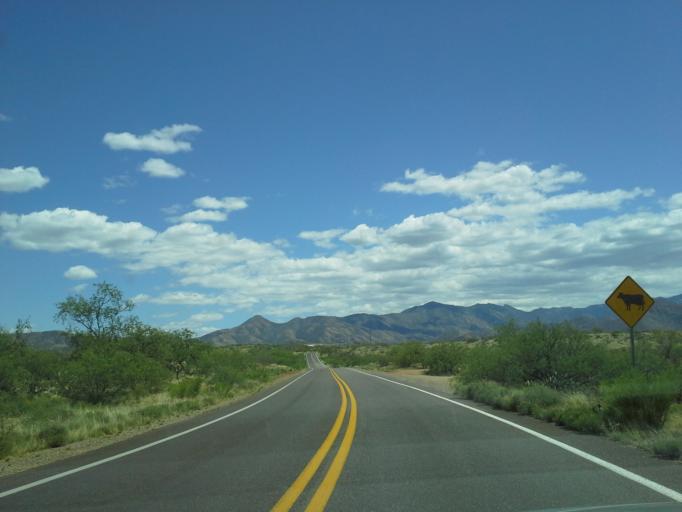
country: US
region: Arizona
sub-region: Pinal County
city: Oracle
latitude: 32.6038
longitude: -110.8608
